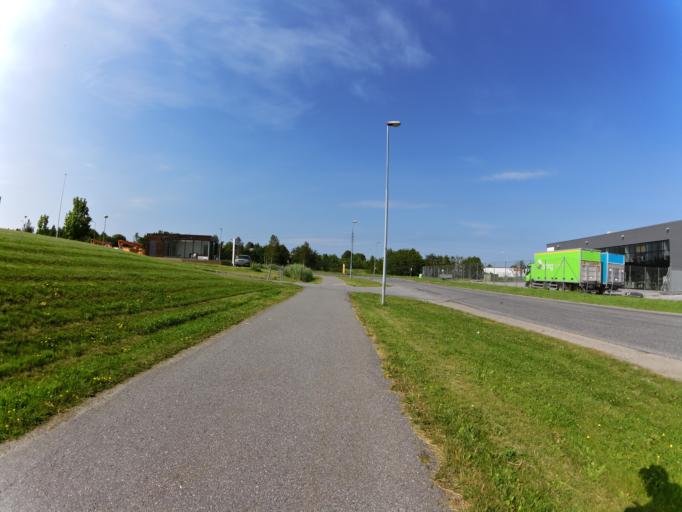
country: NO
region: Ostfold
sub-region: Fredrikstad
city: Fredrikstad
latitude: 59.2388
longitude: 10.9903
